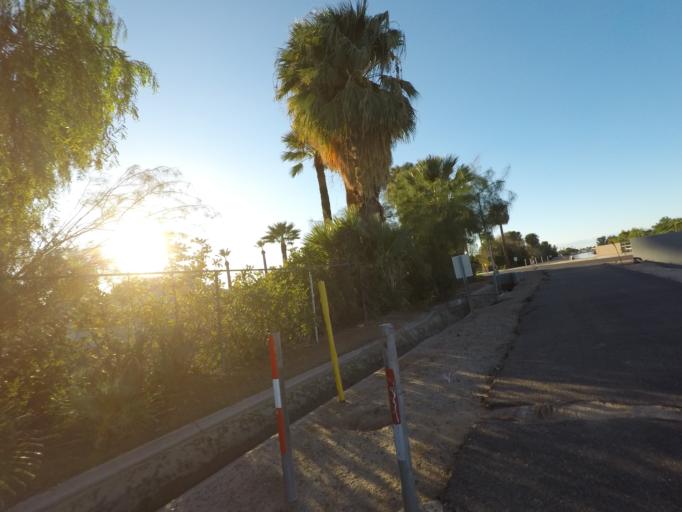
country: US
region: Arizona
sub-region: Maricopa County
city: Phoenix
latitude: 33.4728
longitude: -112.0253
